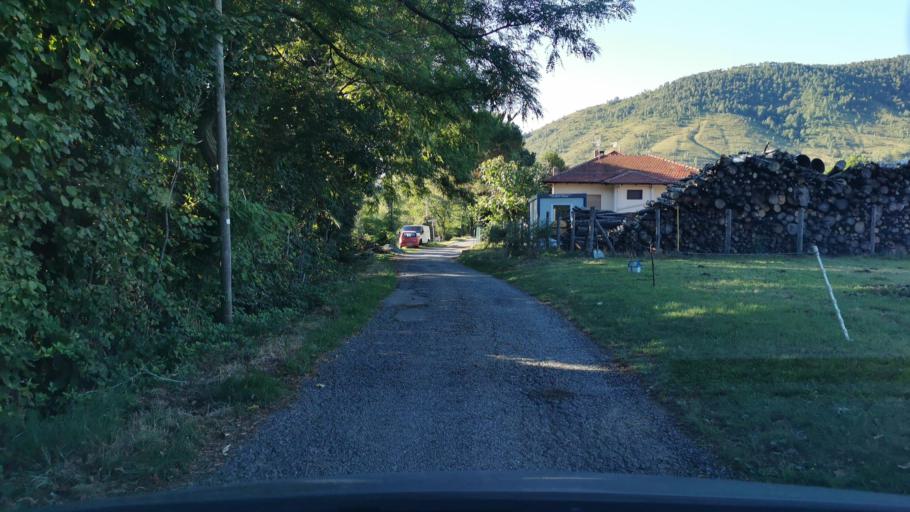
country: IT
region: Piedmont
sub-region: Provincia di Torino
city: Corio
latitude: 45.3082
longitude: 7.5308
